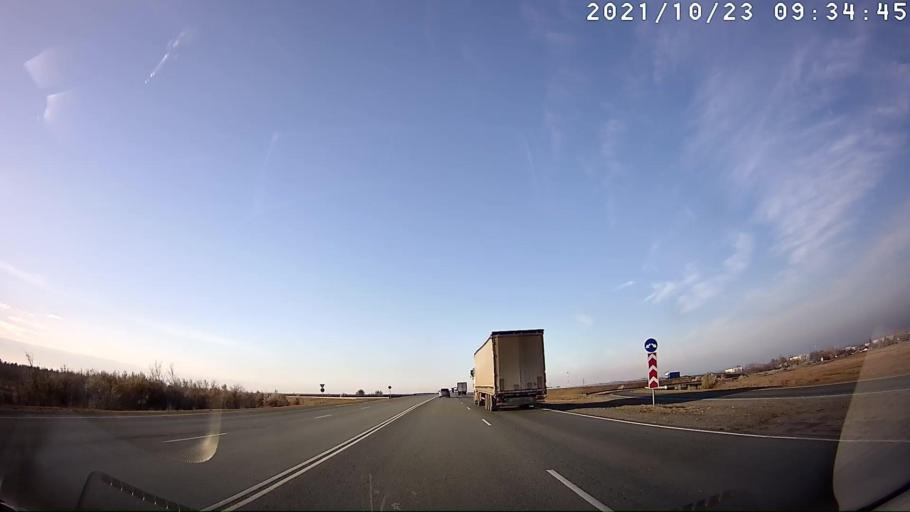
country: RU
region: Saratov
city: Sokolovyy
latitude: 51.6502
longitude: 45.8308
